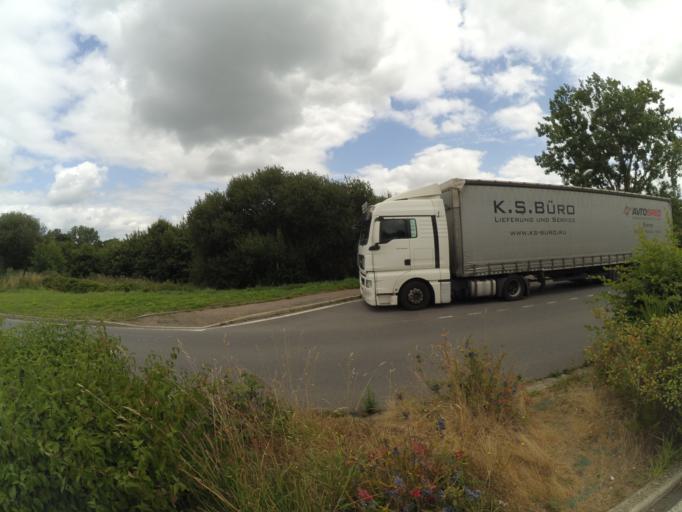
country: FR
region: Brittany
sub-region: Departement des Cotes-d'Armor
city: Plestan
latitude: 48.4192
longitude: -2.4390
